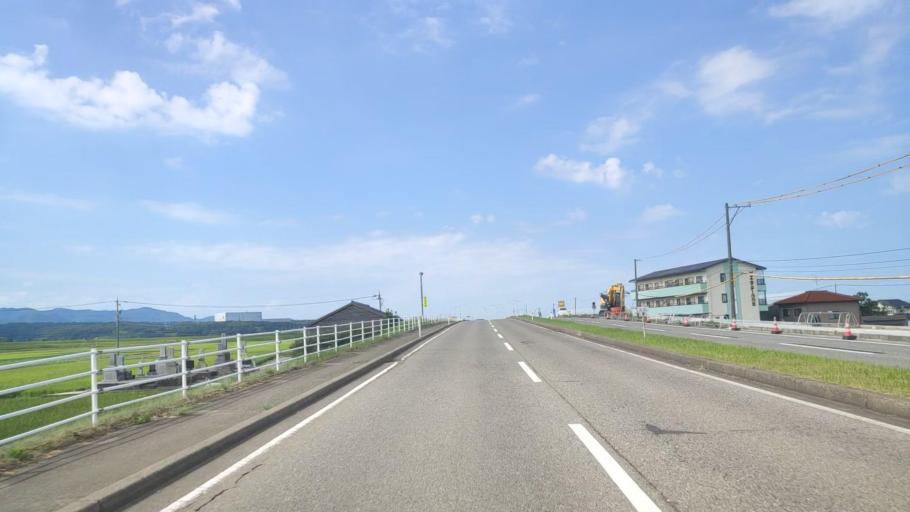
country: JP
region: Ishikawa
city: Matsuto
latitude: 36.4677
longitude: 136.5796
